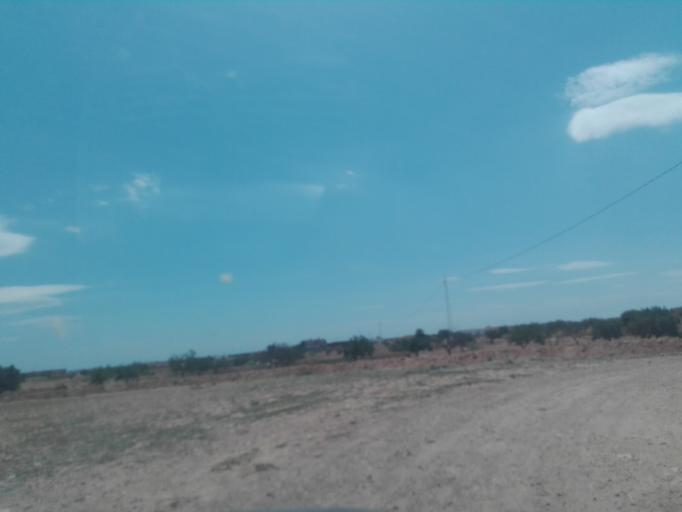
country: TN
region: Safaqis
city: Sfax
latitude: 34.6518
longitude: 10.5948
